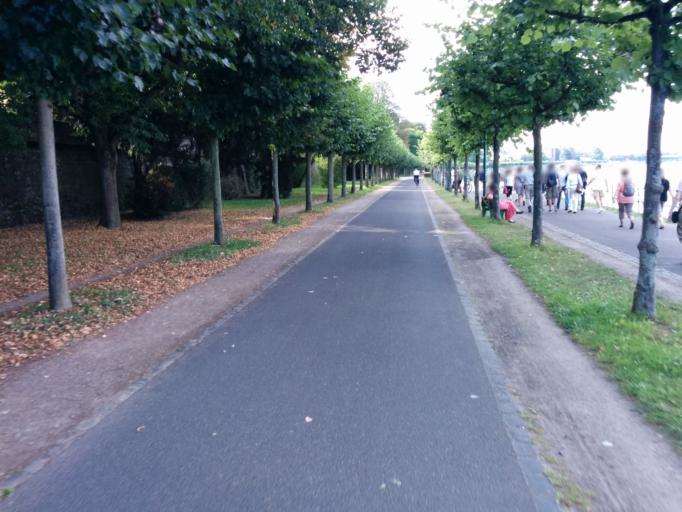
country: DE
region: North Rhine-Westphalia
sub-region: Regierungsbezirk Koln
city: Bonn
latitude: 50.7242
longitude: 7.1169
